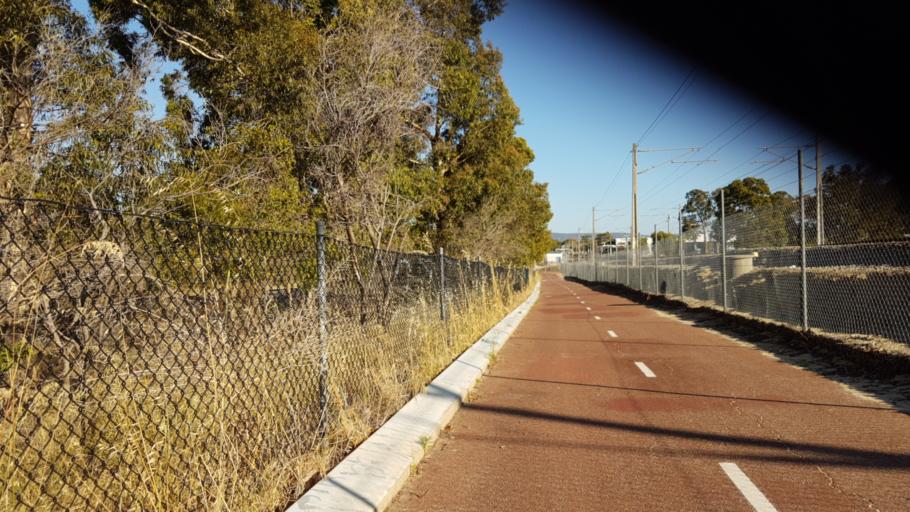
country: AU
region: Western Australia
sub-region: Gosnells
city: Kenwick
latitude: -32.0339
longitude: 115.9671
